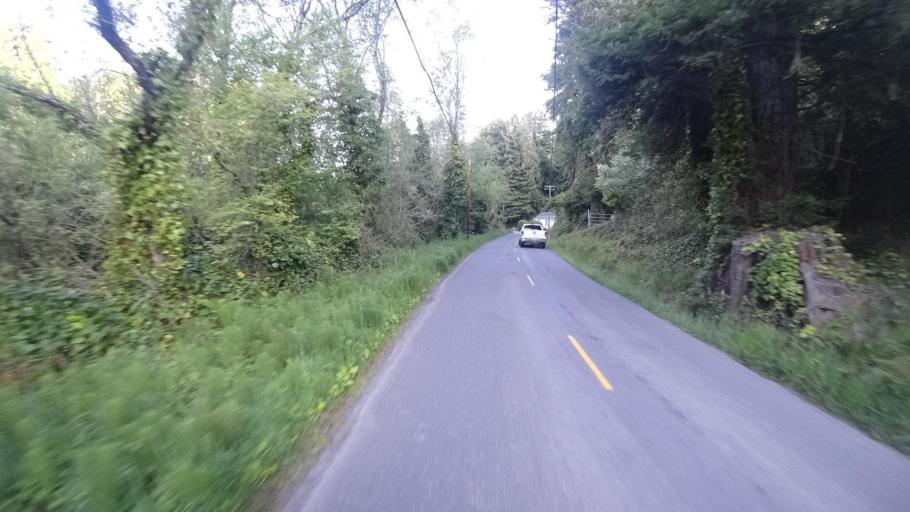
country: US
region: California
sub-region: Humboldt County
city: Myrtletown
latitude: 40.7755
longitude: -124.1129
